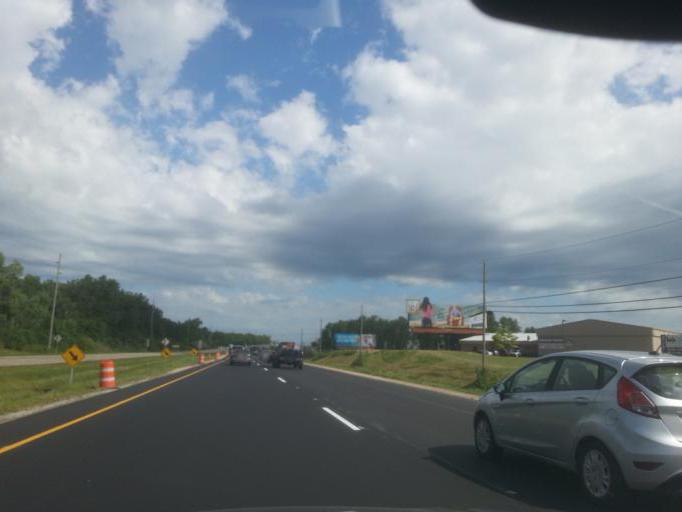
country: US
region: Wisconsin
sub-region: Dane County
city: Monona
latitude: 43.0531
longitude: -89.3085
